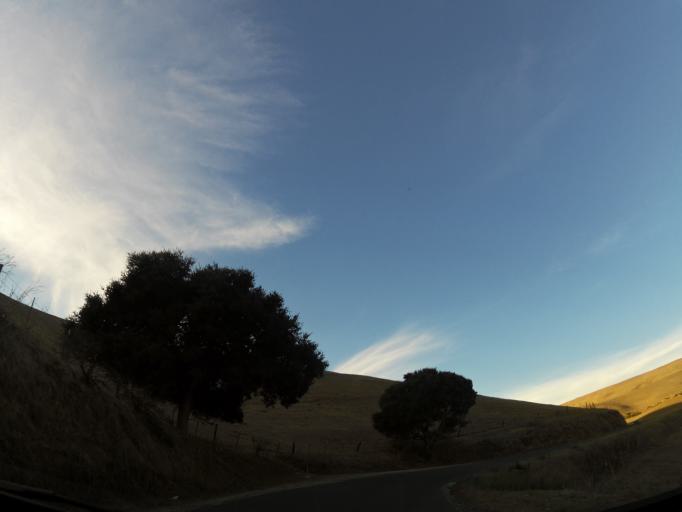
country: US
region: California
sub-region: San Benito County
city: San Juan Bautista
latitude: 36.8081
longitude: -121.5830
